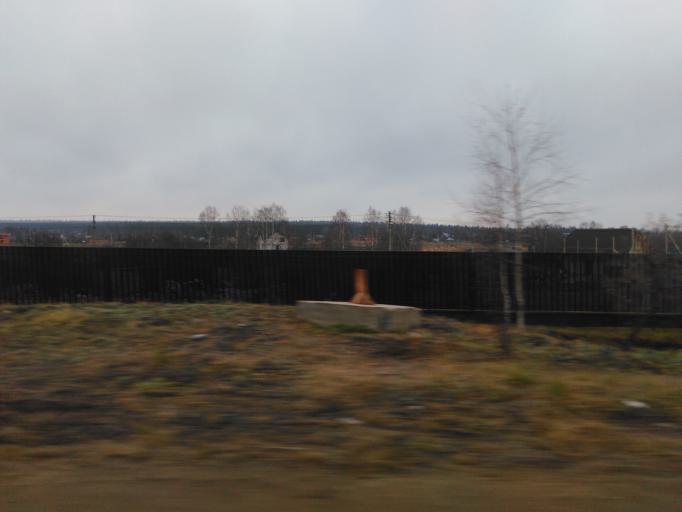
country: RU
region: Moskovskaya
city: Ashukino
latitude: 56.1698
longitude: 37.9399
